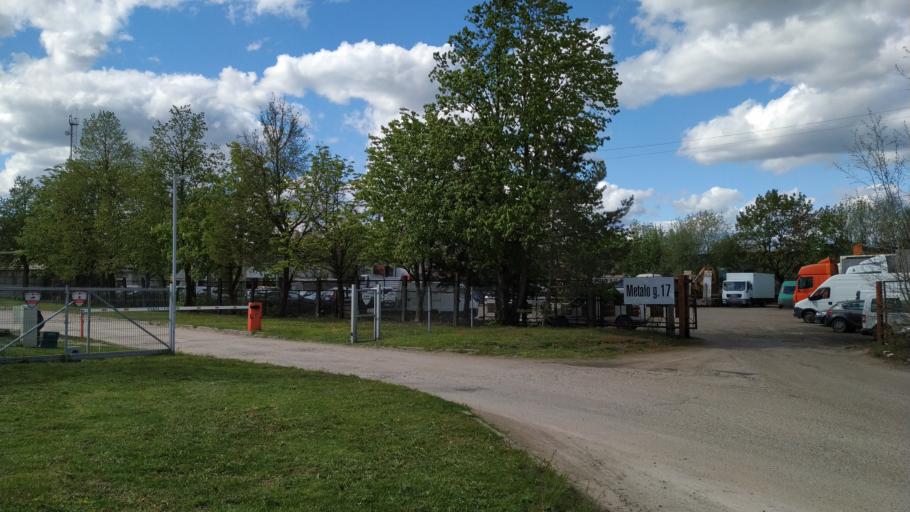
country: LT
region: Vilnius County
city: Vilkpede
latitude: 54.6346
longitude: 25.2614
